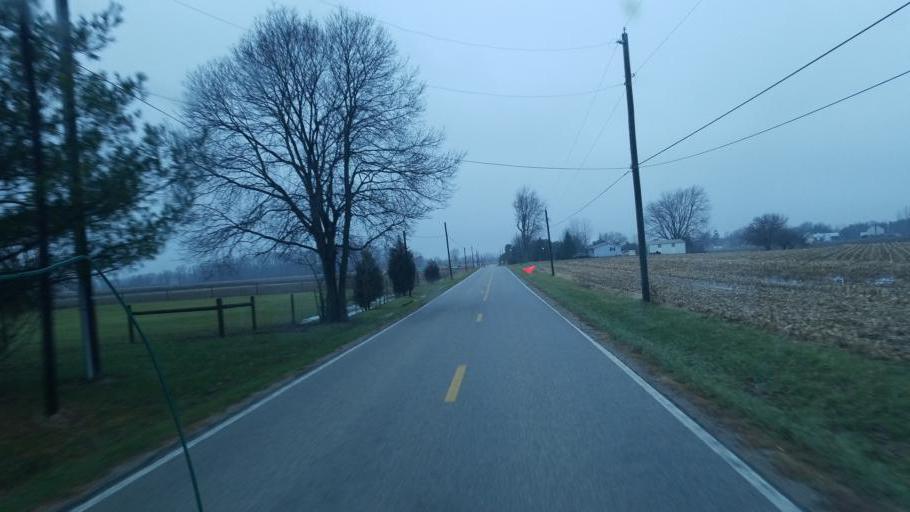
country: US
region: Ohio
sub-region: Delaware County
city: Delaware
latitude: 40.2772
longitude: -83.0240
